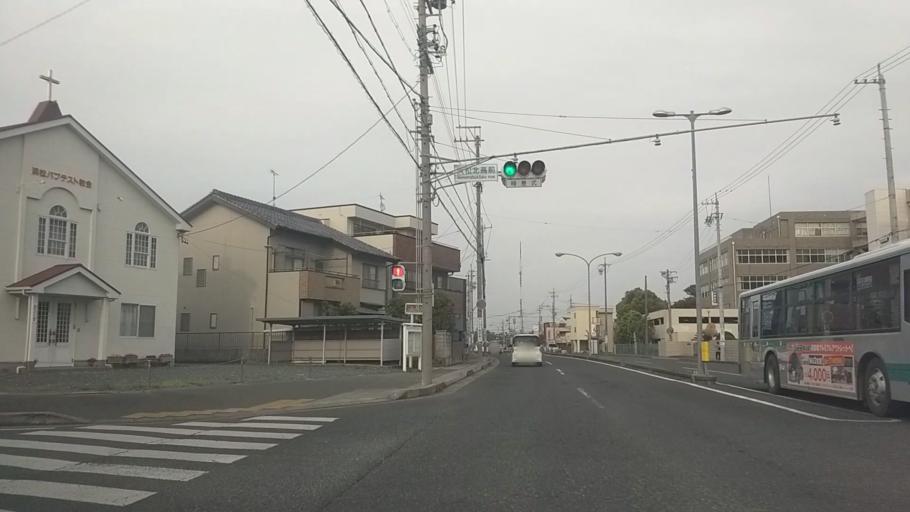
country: JP
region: Shizuoka
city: Hamamatsu
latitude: 34.7188
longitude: 137.7159
